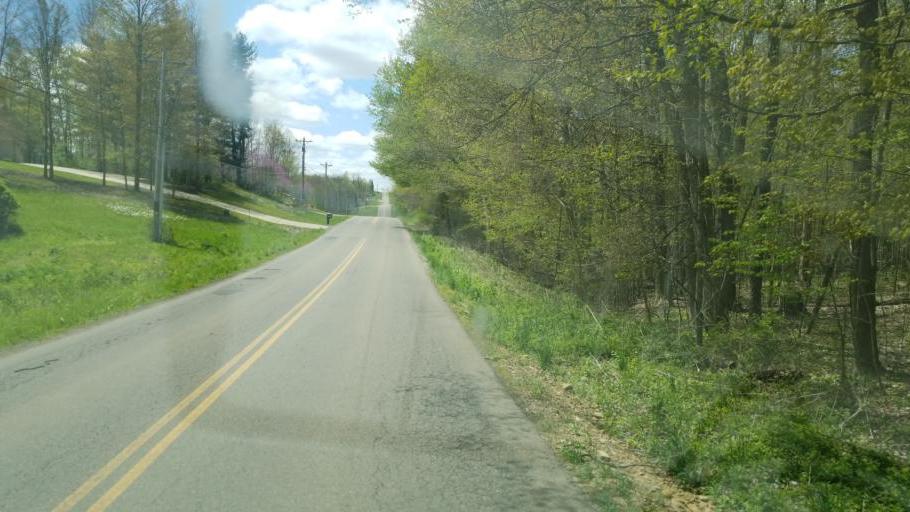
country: US
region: Ohio
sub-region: Knox County
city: Gambier
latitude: 40.4415
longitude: -82.3667
